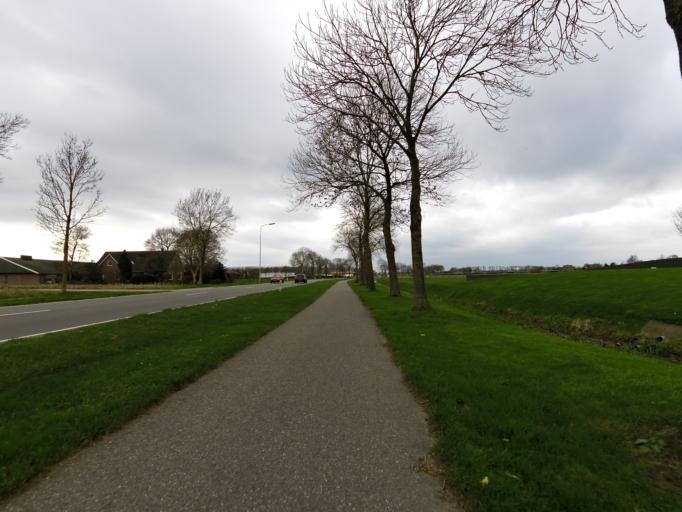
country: NL
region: Gelderland
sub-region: Gemeente Zevenaar
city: Zevenaar
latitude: 51.9371
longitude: 6.1109
